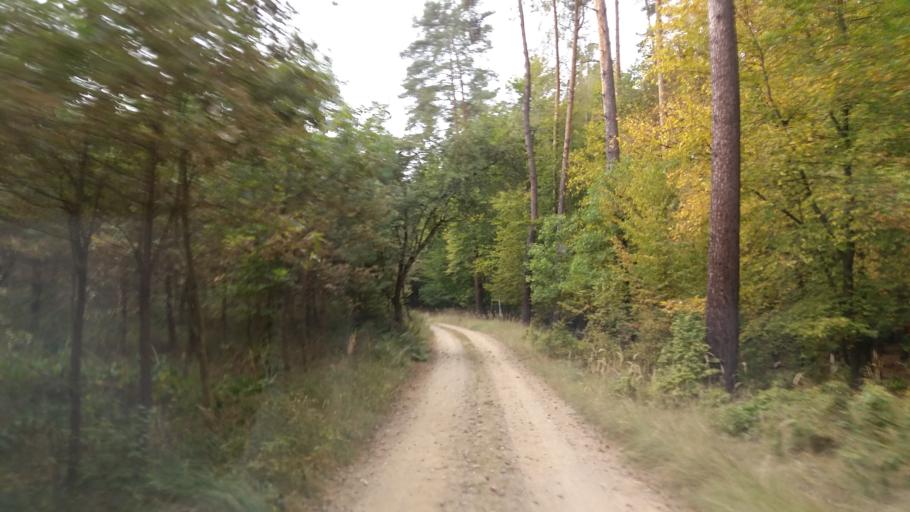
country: PL
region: West Pomeranian Voivodeship
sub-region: Powiat choszczenski
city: Pelczyce
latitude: 52.9589
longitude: 15.3307
